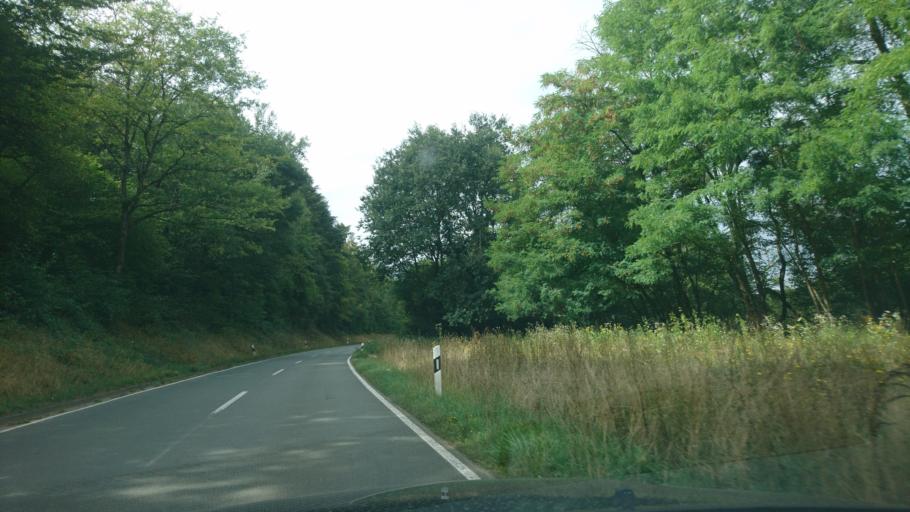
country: DE
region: Rheinland-Pfalz
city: Wiltingen
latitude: 49.6506
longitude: 6.6029
